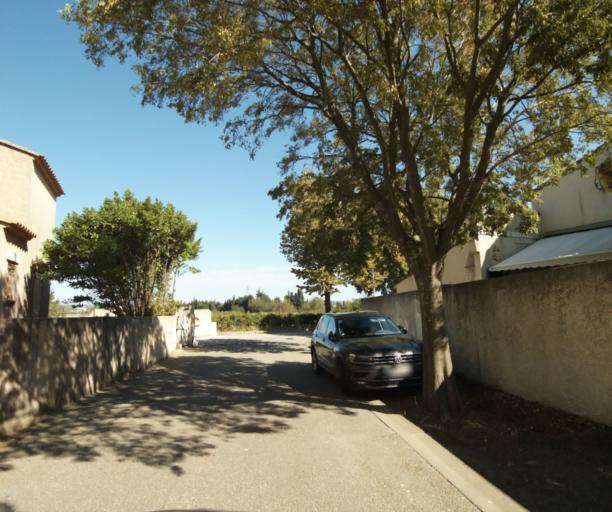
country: FR
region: Languedoc-Roussillon
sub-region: Departement du Gard
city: Bouillargues
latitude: 43.8020
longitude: 4.4178
